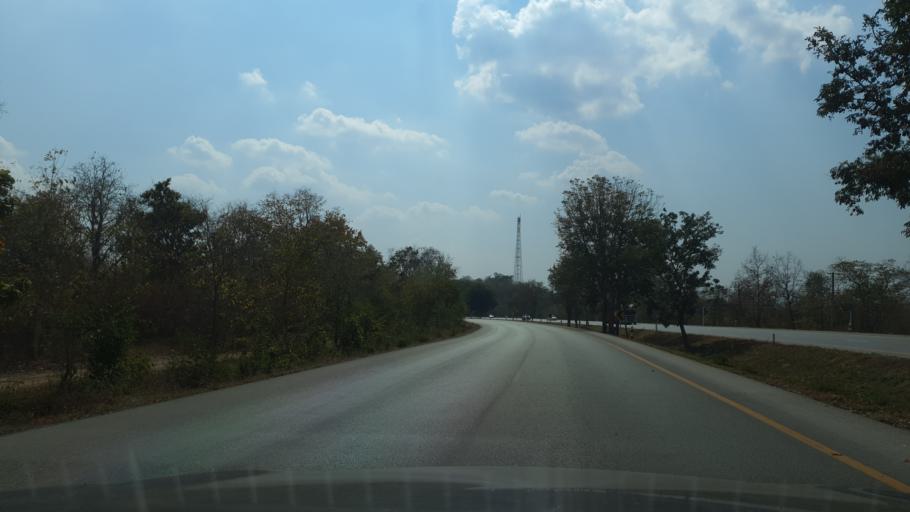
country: TH
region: Lampang
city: Mae Phrik
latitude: 17.4078
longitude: 99.1497
